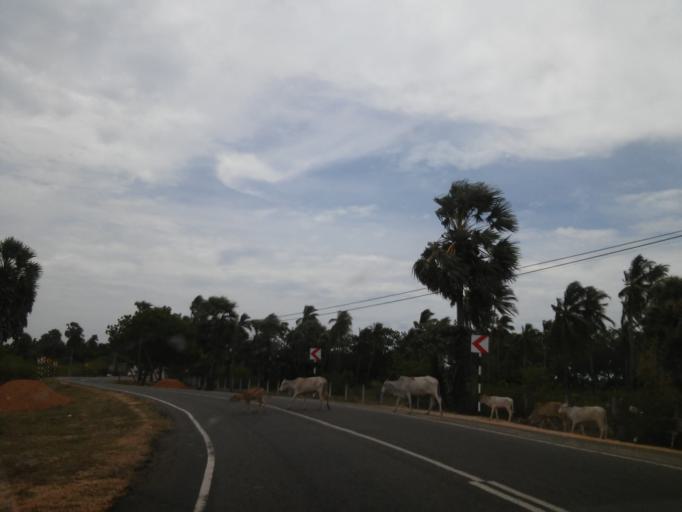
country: LK
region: Eastern Province
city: Trincomalee
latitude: 8.7022
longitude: 81.1799
